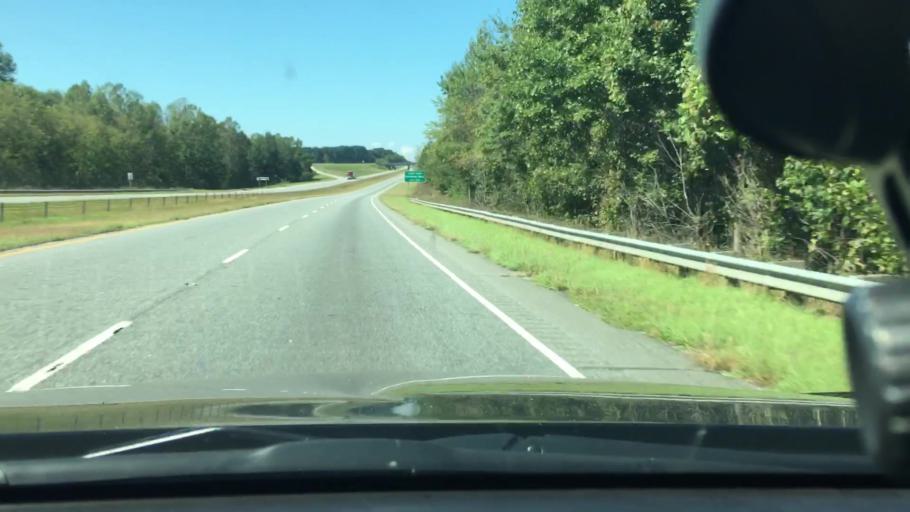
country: US
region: North Carolina
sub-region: Rutherford County
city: Forest City
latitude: 35.3070
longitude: -81.9124
